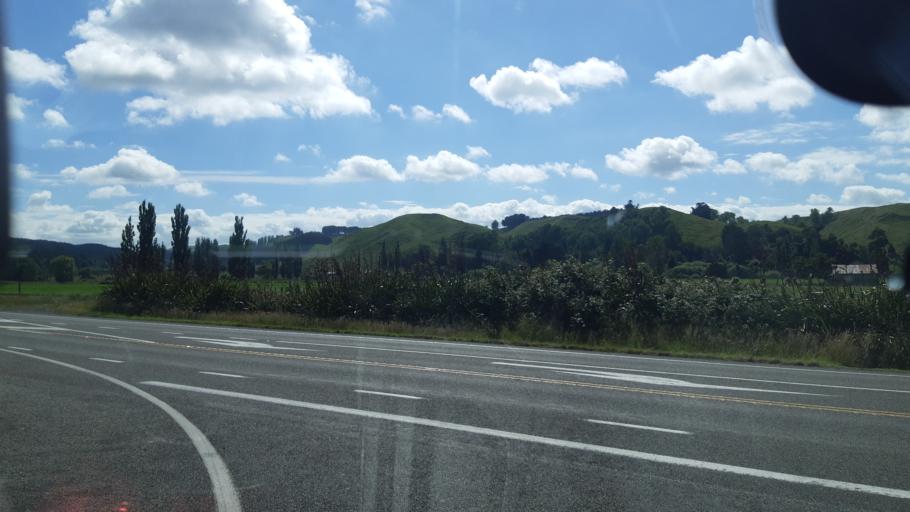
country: NZ
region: Manawatu-Wanganui
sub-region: Rangitikei District
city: Bulls
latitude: -39.9683
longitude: 175.5216
